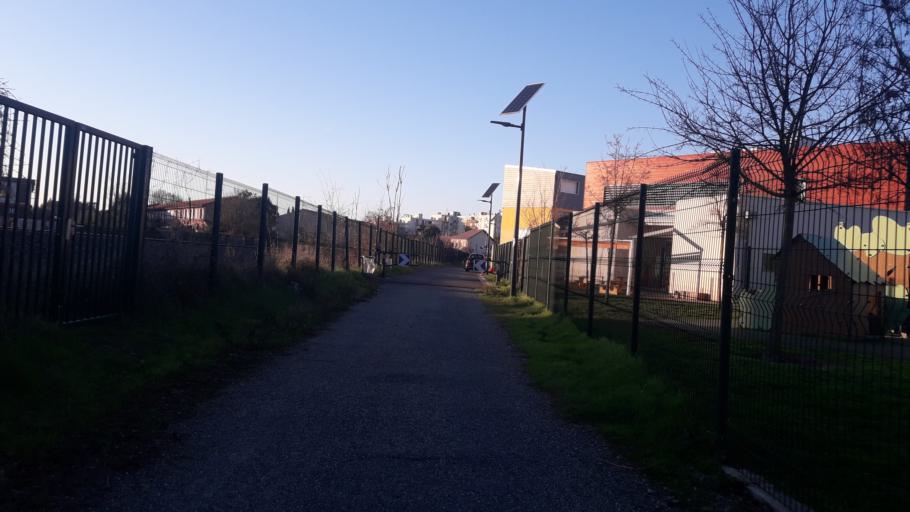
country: FR
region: Midi-Pyrenees
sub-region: Departement de la Haute-Garonne
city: Toulouse
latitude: 43.5712
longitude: 1.4213
